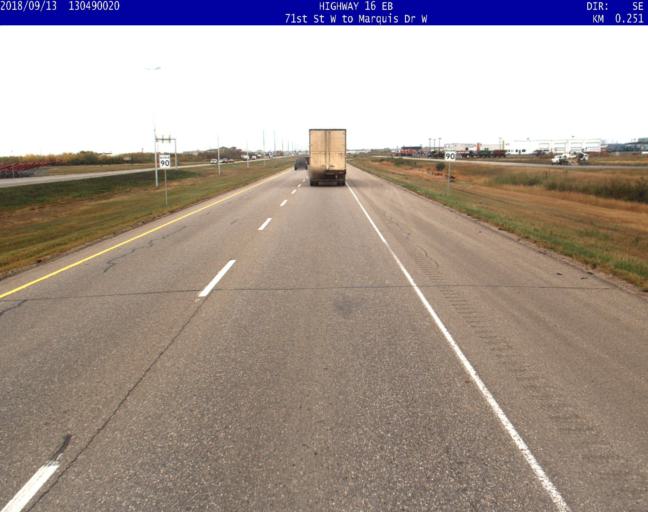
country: CA
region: Saskatchewan
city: Martensville
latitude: 52.2005
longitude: -106.7024
